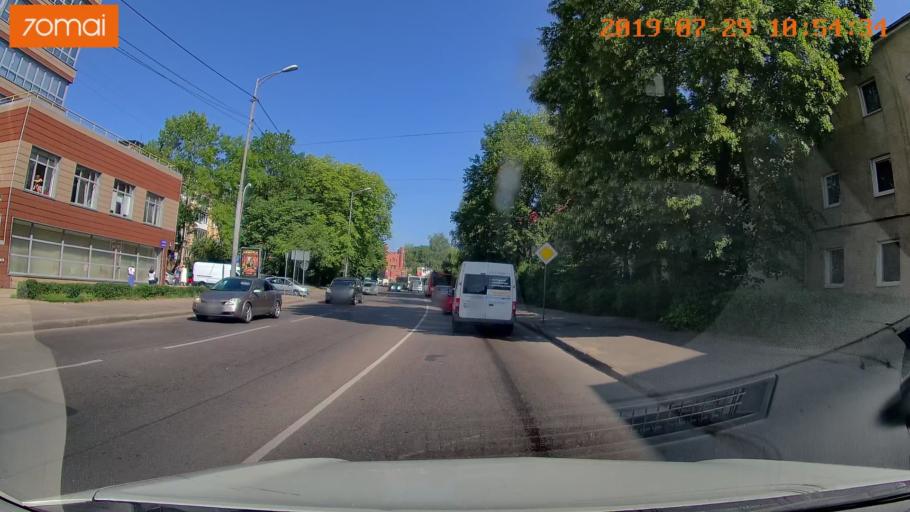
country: RU
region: Kaliningrad
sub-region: Gorod Kaliningrad
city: Kaliningrad
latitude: 54.7114
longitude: 20.5373
